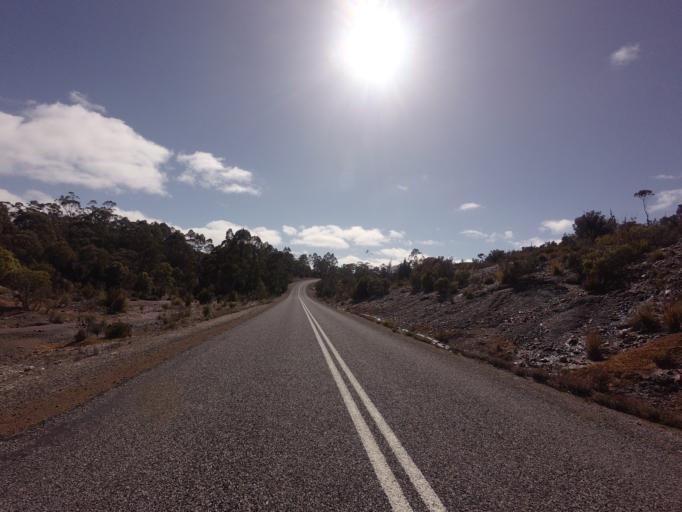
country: AU
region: Tasmania
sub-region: Derwent Valley
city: New Norfolk
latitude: -42.7601
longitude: 146.3974
